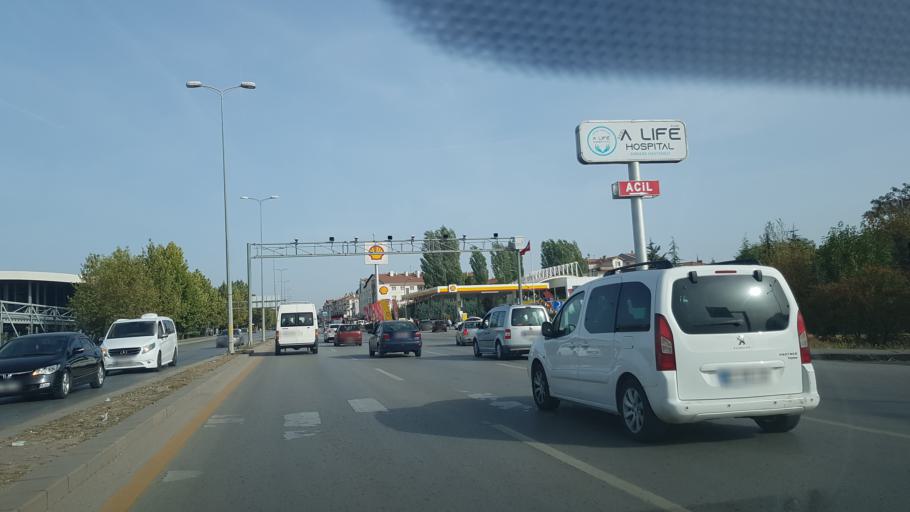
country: TR
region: Ankara
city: Etimesgut
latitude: 39.9558
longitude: 32.6272
